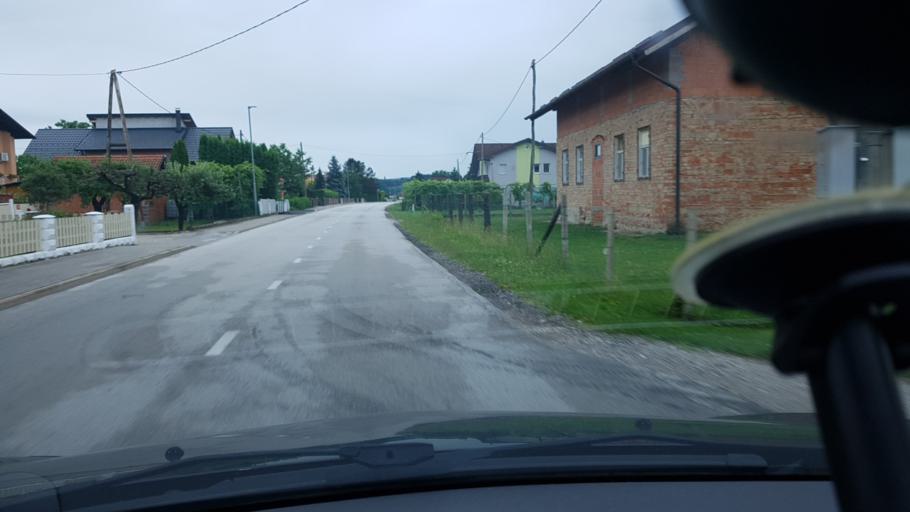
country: SI
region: Videm
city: Videm pri Ptuju
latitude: 46.3851
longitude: 15.8755
